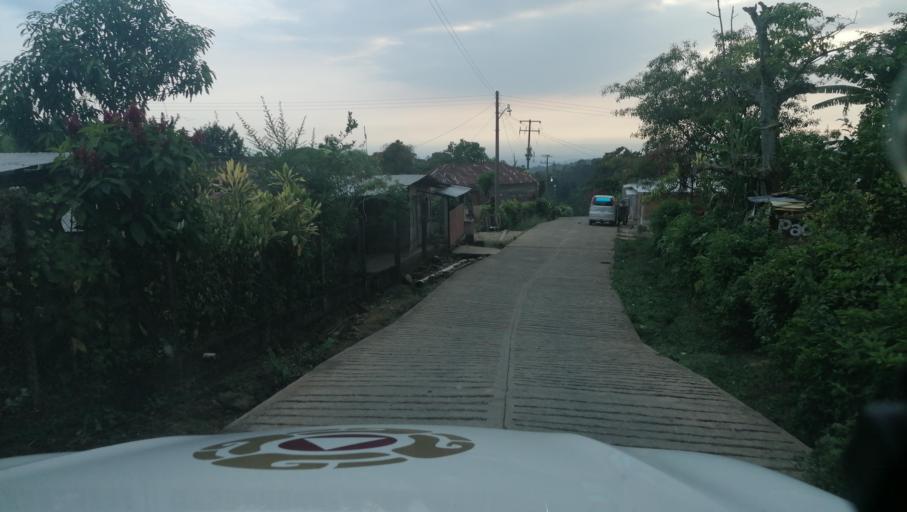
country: MX
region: Chiapas
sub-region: Cacahoatan
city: Benito Juarez
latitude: 15.1039
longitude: -92.2164
